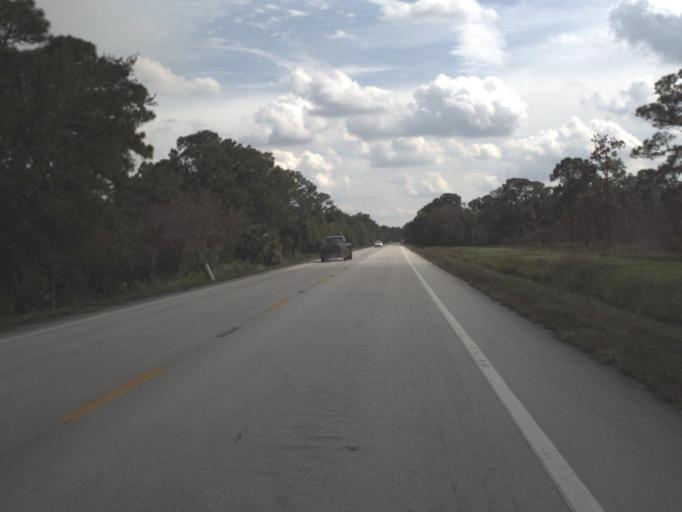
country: US
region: Florida
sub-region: Indian River County
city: Fellsmere
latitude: 27.5883
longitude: -80.8404
